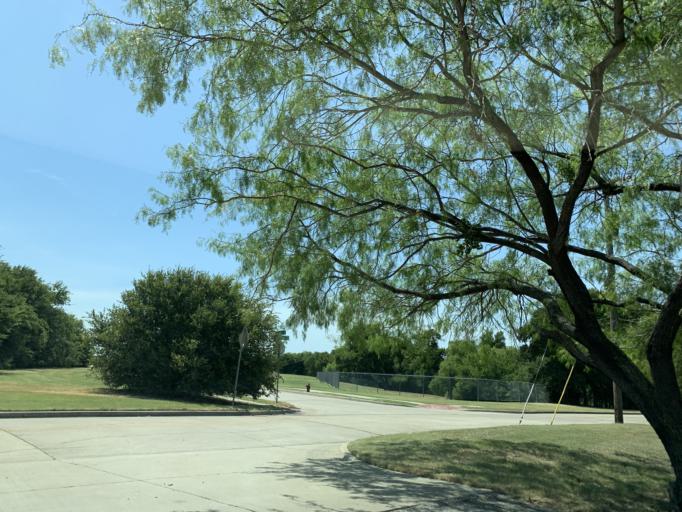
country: US
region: Texas
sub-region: Dallas County
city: Cedar Hill
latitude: 32.6418
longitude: -97.0134
